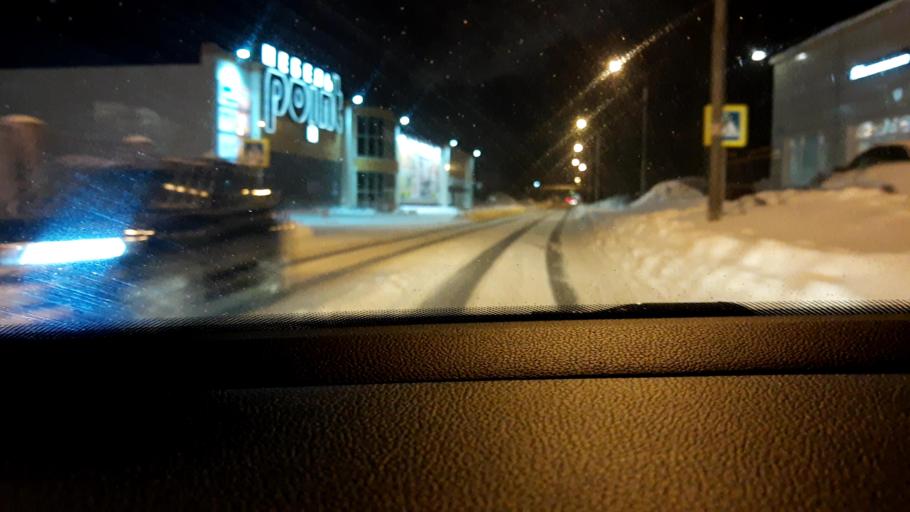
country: RU
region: Moskovskaya
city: Ivanteyevka
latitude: 55.9622
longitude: 37.9324
